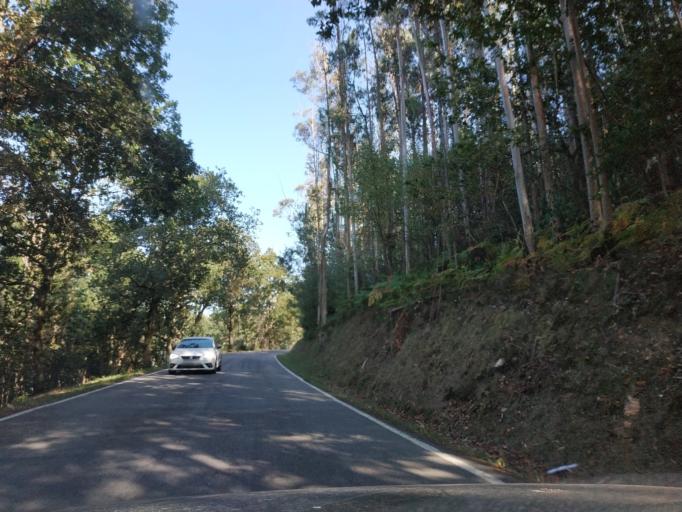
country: ES
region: Galicia
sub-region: Provincia da Coruna
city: Cerceda
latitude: 43.2333
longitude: -8.4700
